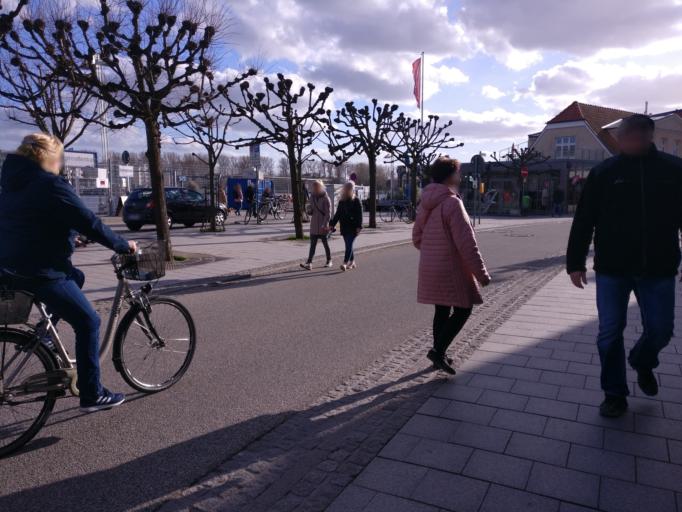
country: DE
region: Schleswig-Holstein
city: Travemuende
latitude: 53.9570
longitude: 10.8698
